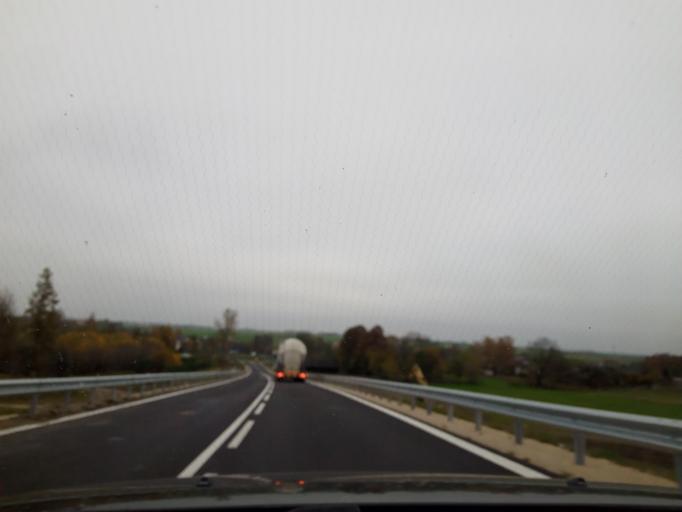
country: PL
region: Swietokrzyskie
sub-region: Powiat jedrzejowski
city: Jedrzejow
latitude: 50.6280
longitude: 20.3262
